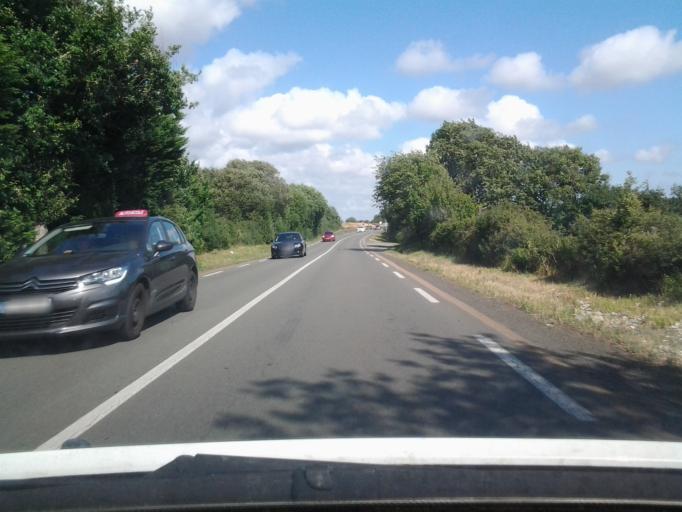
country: FR
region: Pays de la Loire
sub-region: Departement de la Vendee
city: Chateau-d'Olonne
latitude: 46.5262
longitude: -1.7413
